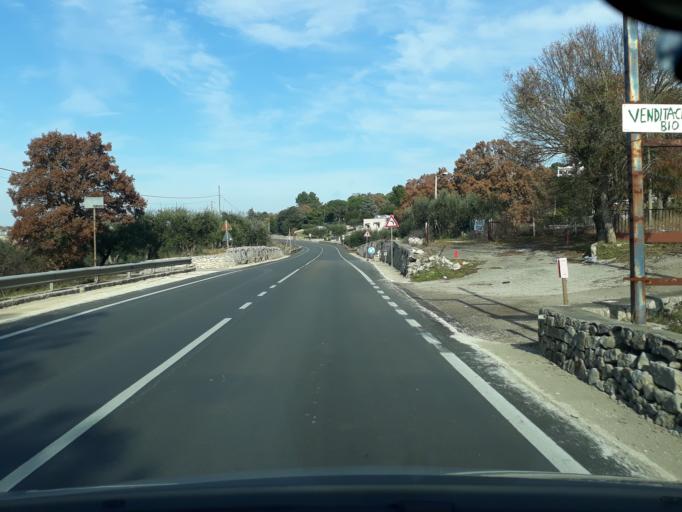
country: IT
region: Apulia
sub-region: Provincia di Bari
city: Locorotondo
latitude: 40.7788
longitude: 17.3377
